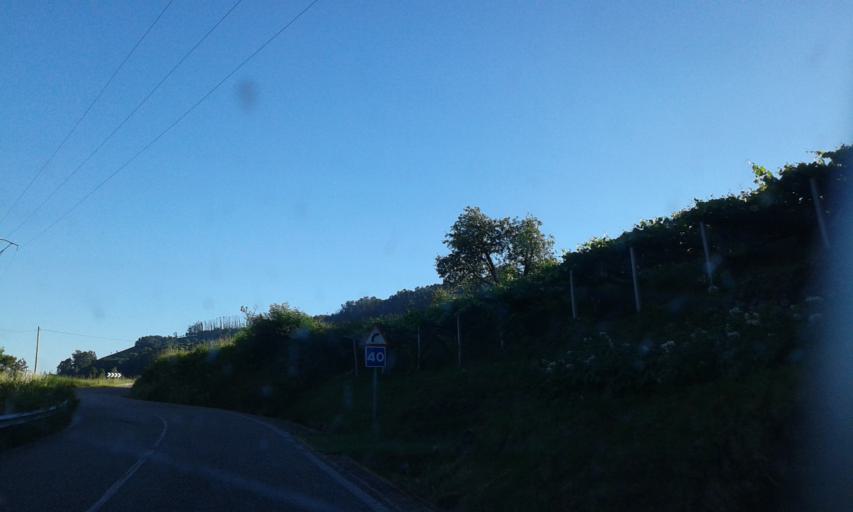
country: ES
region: Galicia
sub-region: Provincia de Pontevedra
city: Oia
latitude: 41.9946
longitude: -8.8184
